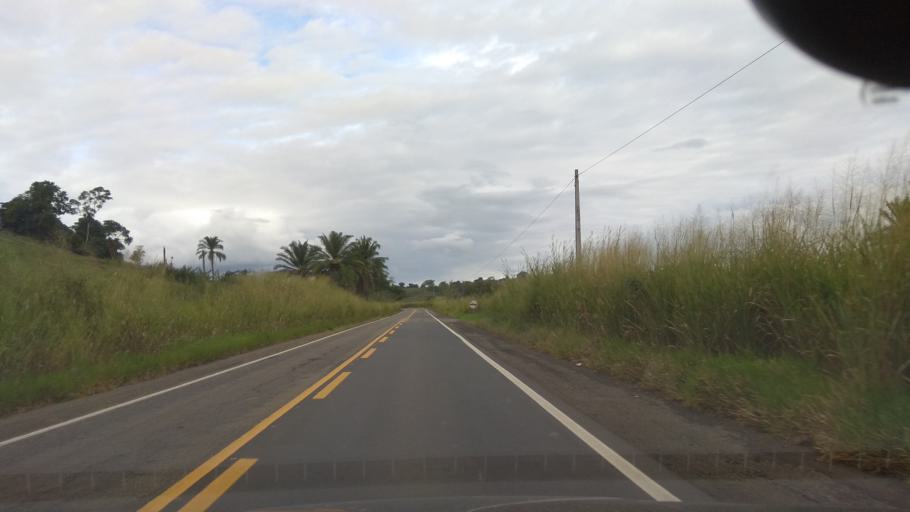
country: BR
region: Bahia
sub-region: Ipiau
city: Ipiau
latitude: -14.1850
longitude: -39.6611
